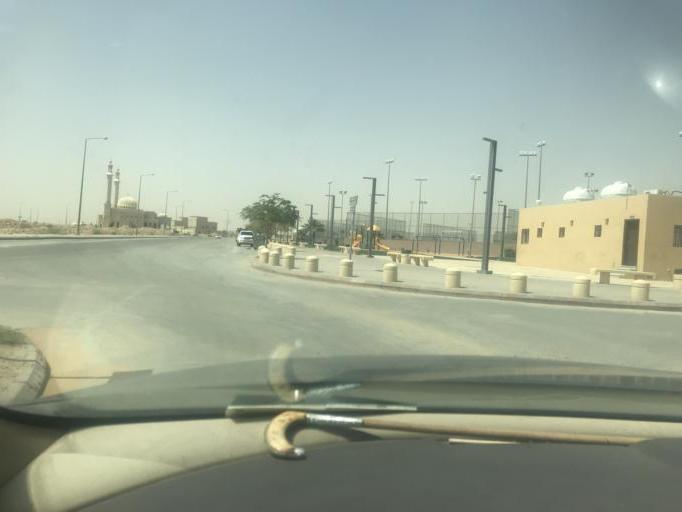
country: SA
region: Ar Riyad
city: Riyadh
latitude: 24.7878
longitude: 46.5807
